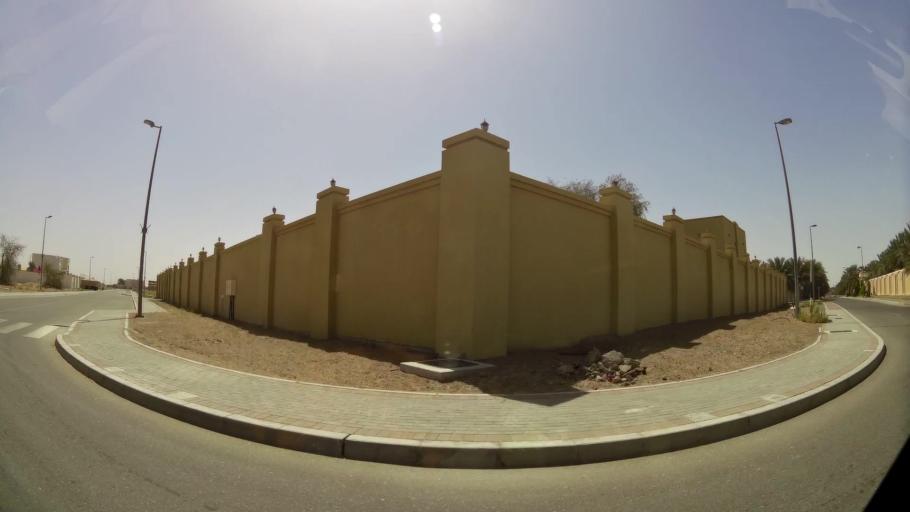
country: OM
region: Al Buraimi
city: Al Buraymi
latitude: 24.3033
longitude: 55.7522
